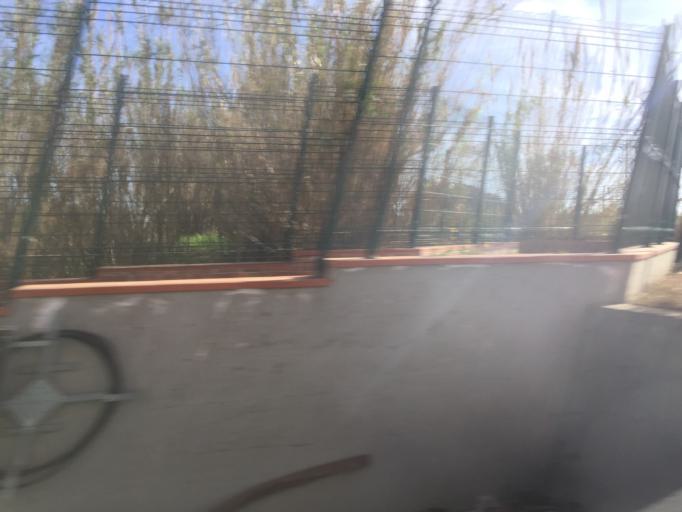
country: IT
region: Latium
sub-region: Citta metropolitana di Roma Capitale
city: Ponte Galeria-La Pisana
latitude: 41.8185
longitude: 12.3421
